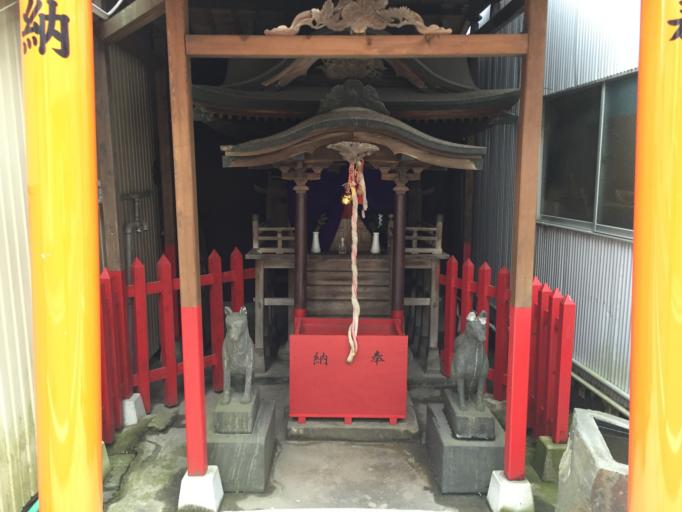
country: JP
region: Miyagi
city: Ishinomaki
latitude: 38.4333
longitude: 141.3050
